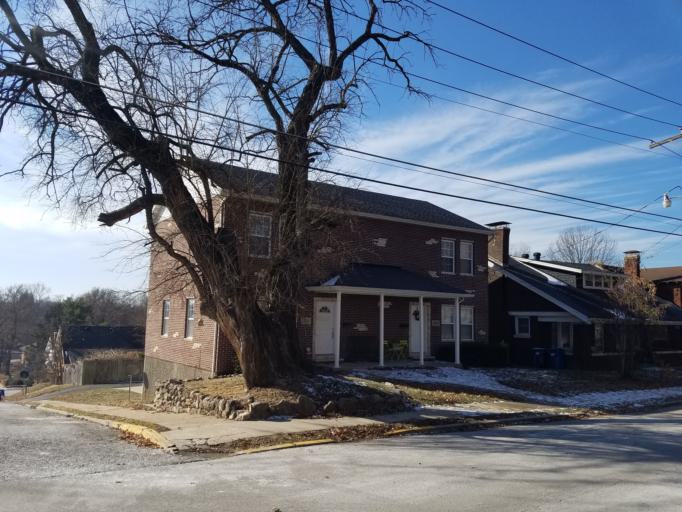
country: US
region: Missouri
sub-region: Cole County
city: Jefferson City
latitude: 38.5873
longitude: -92.1861
